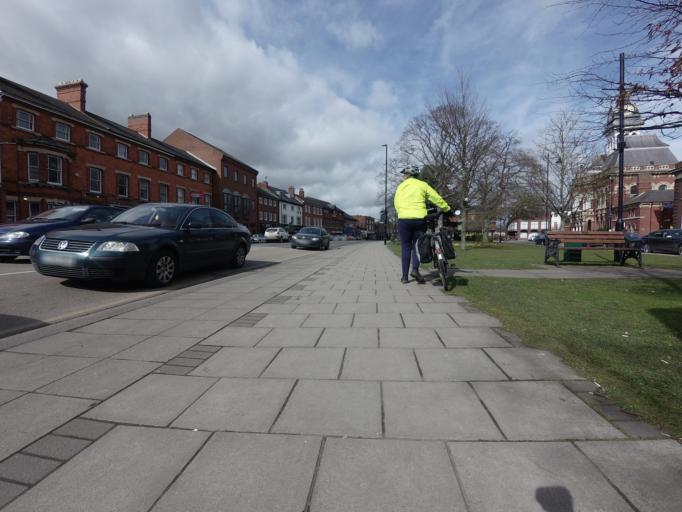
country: GB
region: England
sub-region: Lincolnshire
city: Grantham
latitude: 52.9100
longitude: -0.6404
